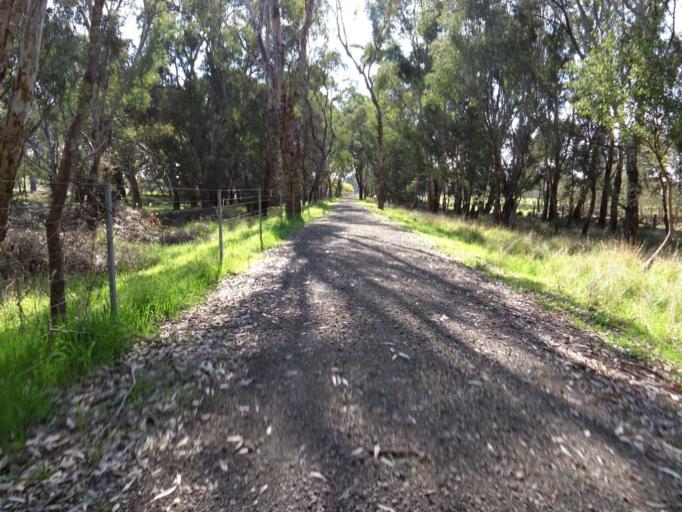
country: AU
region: Victoria
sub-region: Murrindindi
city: Alexandra
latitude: -37.1544
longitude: 145.5757
